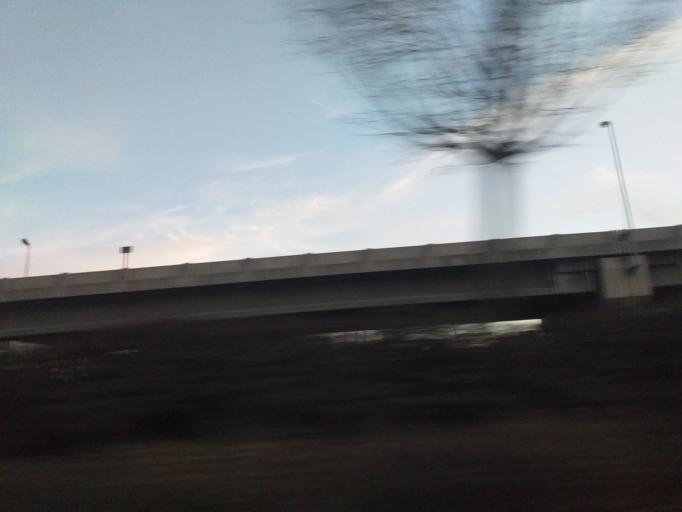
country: TR
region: Ankara
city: Ankara
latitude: 39.9552
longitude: 32.8255
